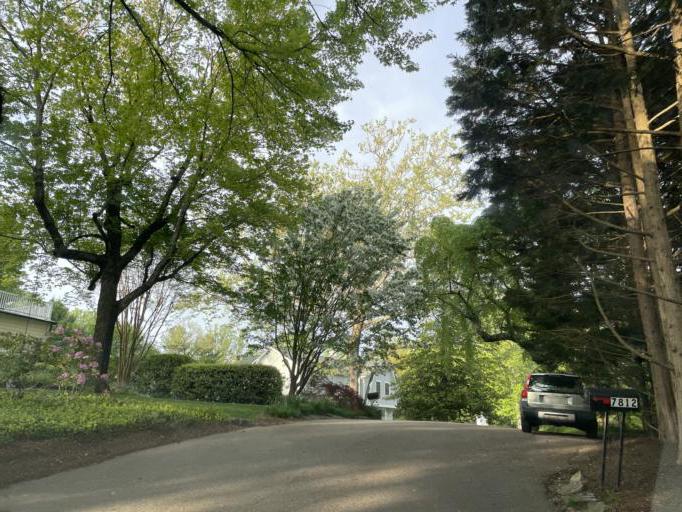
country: US
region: Maryland
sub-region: Baltimore County
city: Lutherville
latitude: 39.4045
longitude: -76.6396
